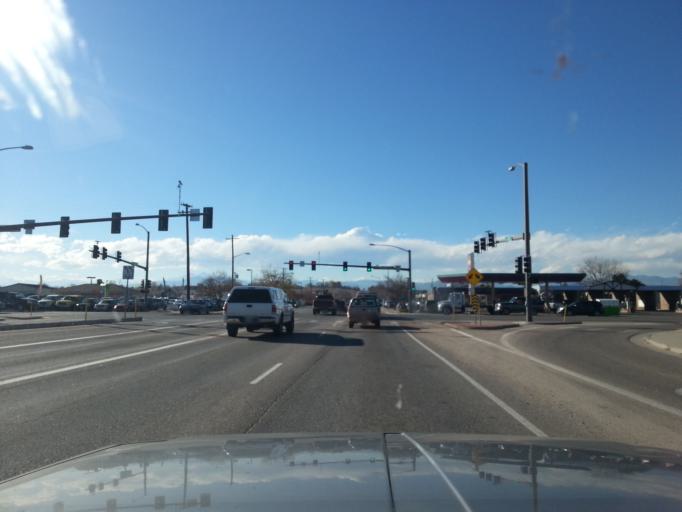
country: US
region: Colorado
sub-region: Larimer County
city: Loveland
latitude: 40.3784
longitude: -105.0728
